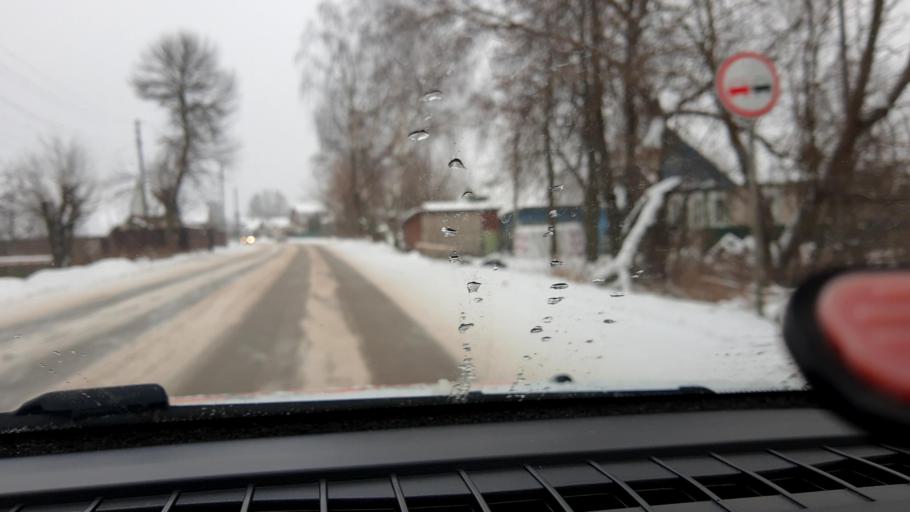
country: RU
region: Nizjnij Novgorod
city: Afonino
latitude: 56.3184
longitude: 44.1685
